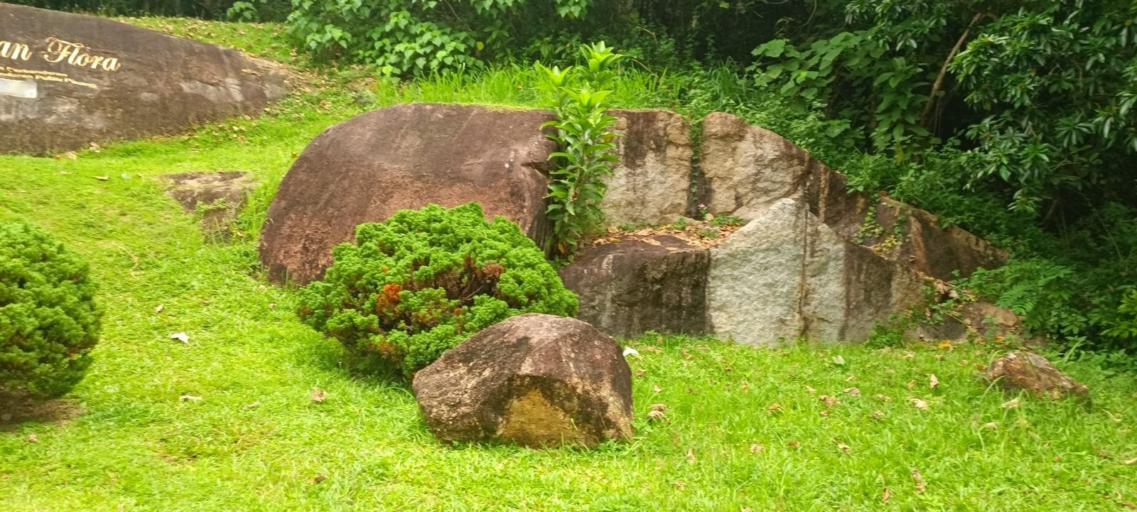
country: MY
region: Penang
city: Tanjung Tokong
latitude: 5.4279
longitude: 100.2958
